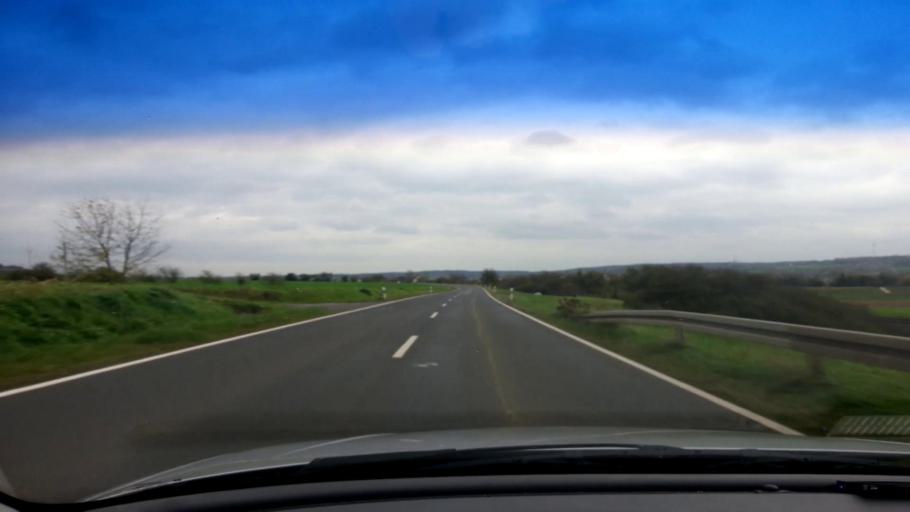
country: DE
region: Bavaria
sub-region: Regierungsbezirk Unterfranken
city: Stettfeld
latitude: 49.9564
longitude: 10.7377
